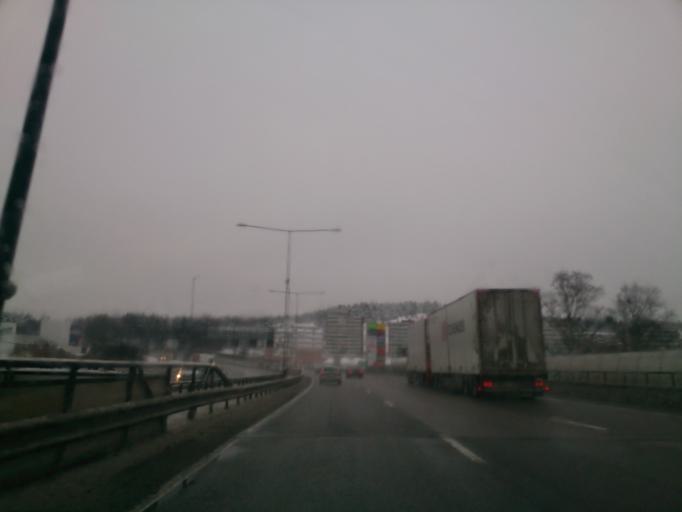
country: SE
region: Stockholm
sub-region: Botkyrka Kommun
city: Fittja
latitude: 59.2543
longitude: 17.8727
